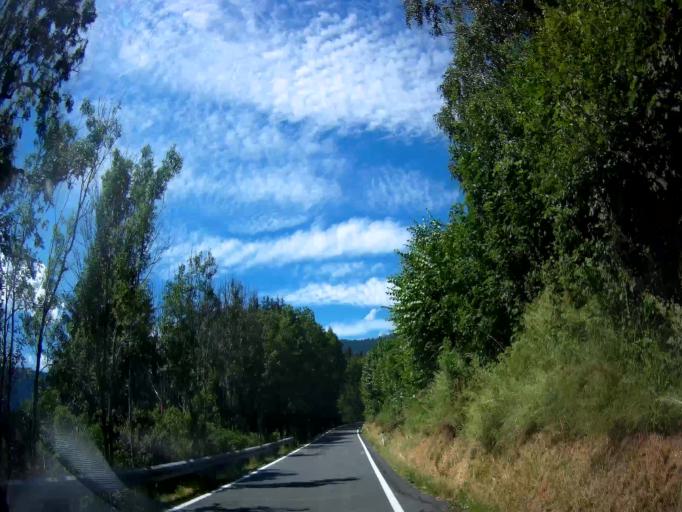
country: AT
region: Carinthia
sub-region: Politischer Bezirk Sankt Veit an der Glan
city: Glodnitz
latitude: 46.9106
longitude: 14.0929
